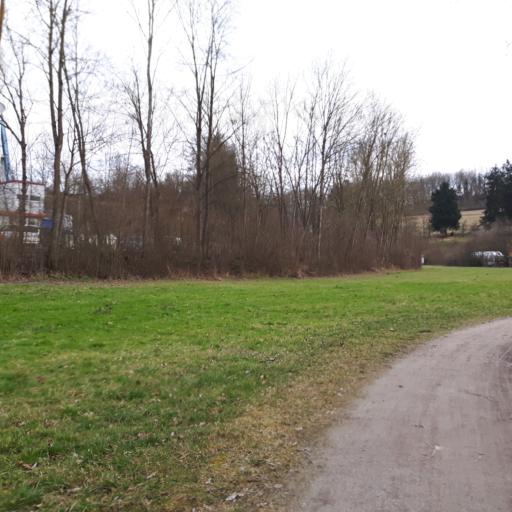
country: DE
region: Baden-Wuerttemberg
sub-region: Regierungsbezirk Stuttgart
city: Neckarwestheim
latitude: 49.0545
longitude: 9.2168
